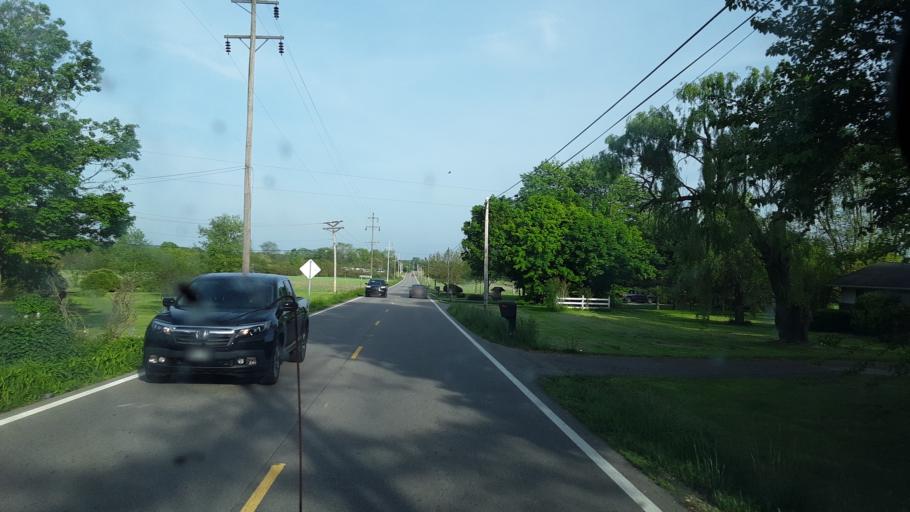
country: US
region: Ohio
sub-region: Pickaway County
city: Logan Elm Village
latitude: 39.5631
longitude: -82.8830
